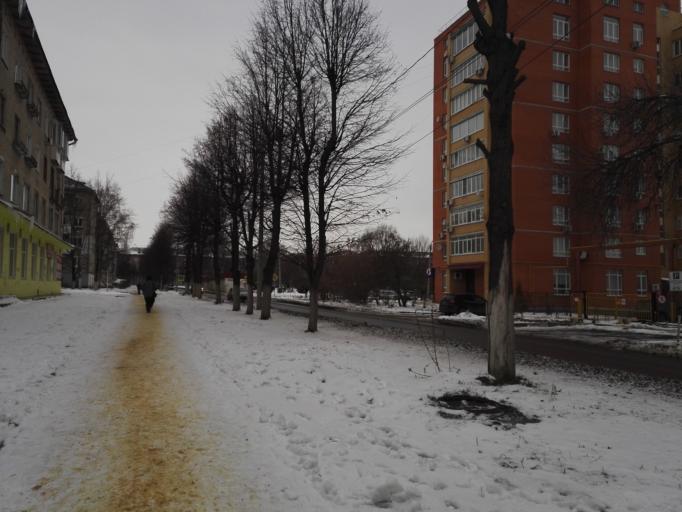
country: RU
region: Tula
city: Novomoskovsk
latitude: 54.0102
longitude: 38.3081
